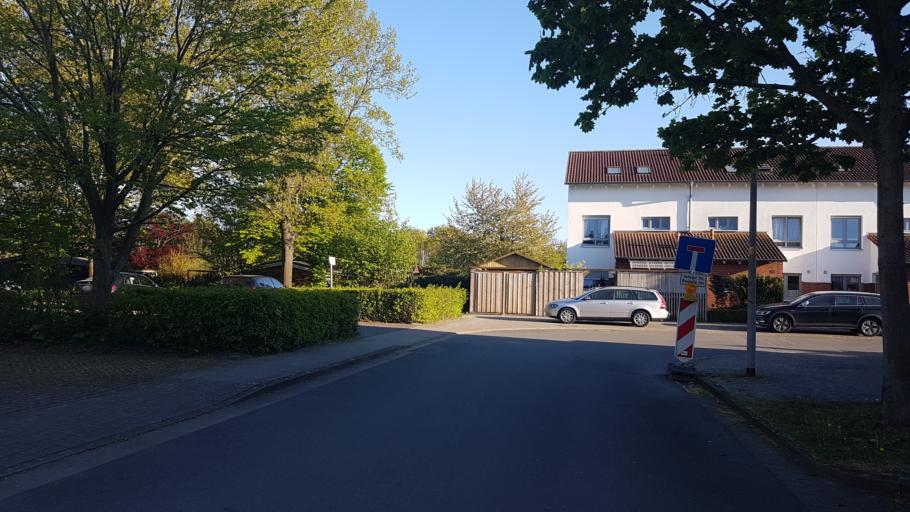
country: DE
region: Lower Saxony
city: Hannover
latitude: 52.3939
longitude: 9.8076
